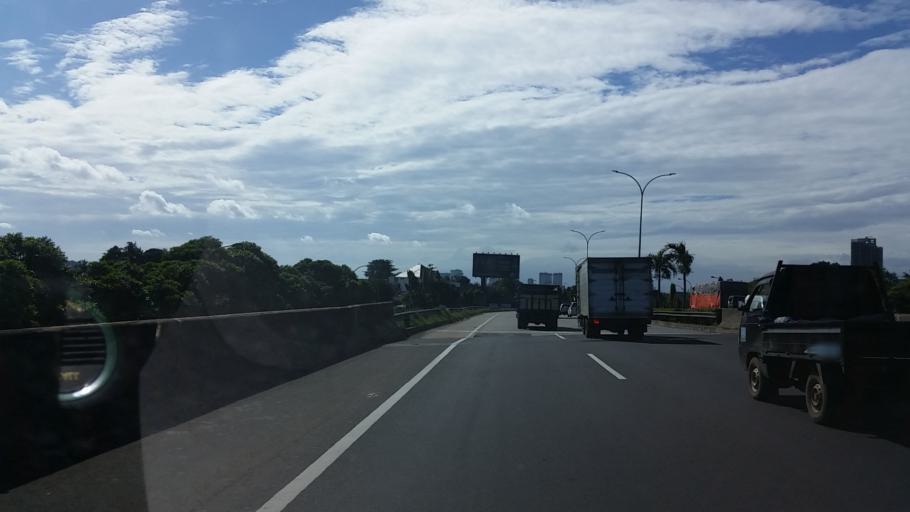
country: ID
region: Banten
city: South Tangerang
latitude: -6.2617
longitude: 106.7670
